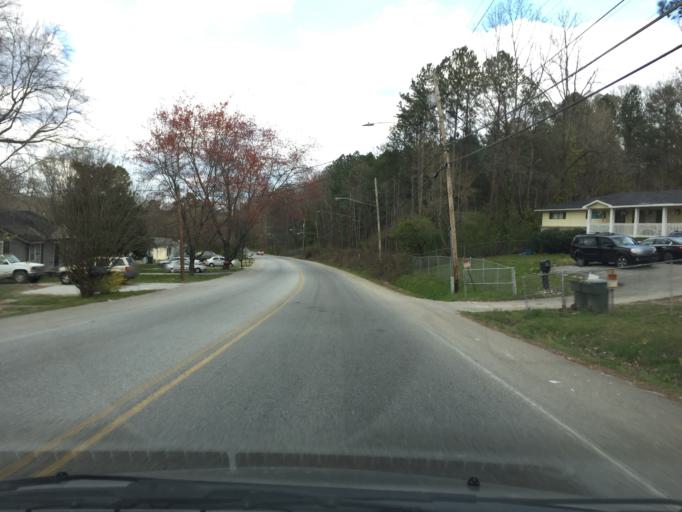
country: US
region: Tennessee
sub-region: Hamilton County
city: East Chattanooga
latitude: 35.0758
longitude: -85.2310
